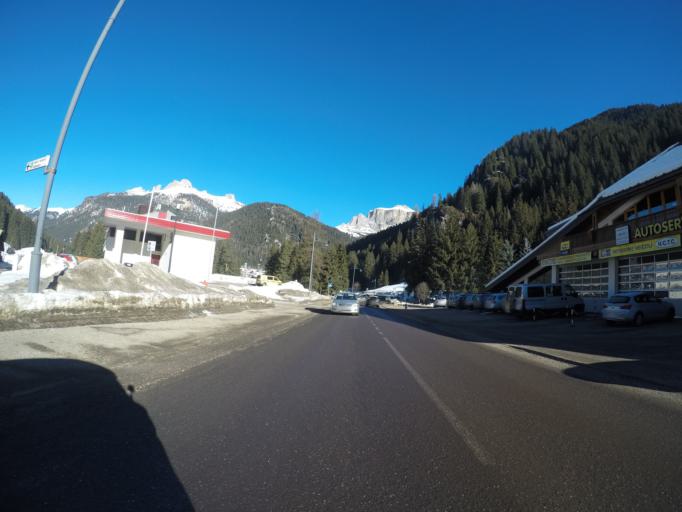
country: IT
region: Trentino-Alto Adige
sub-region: Provincia di Trento
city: Canazei
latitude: 46.4695
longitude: 11.7786
